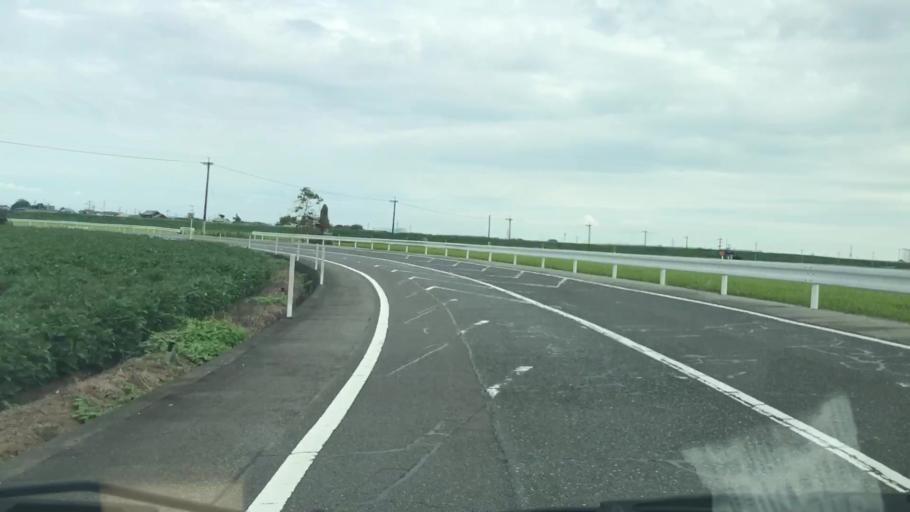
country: JP
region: Saga Prefecture
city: Saga-shi
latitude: 33.2890
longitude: 130.2406
